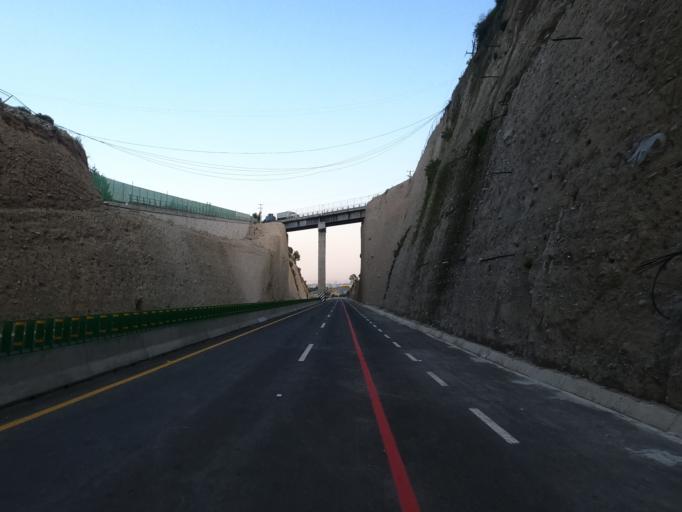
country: MX
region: Mexico
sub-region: Naucalpan de Juarez
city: Llano de las Flores (Barrio del Hueso)
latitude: 19.4231
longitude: -99.3283
